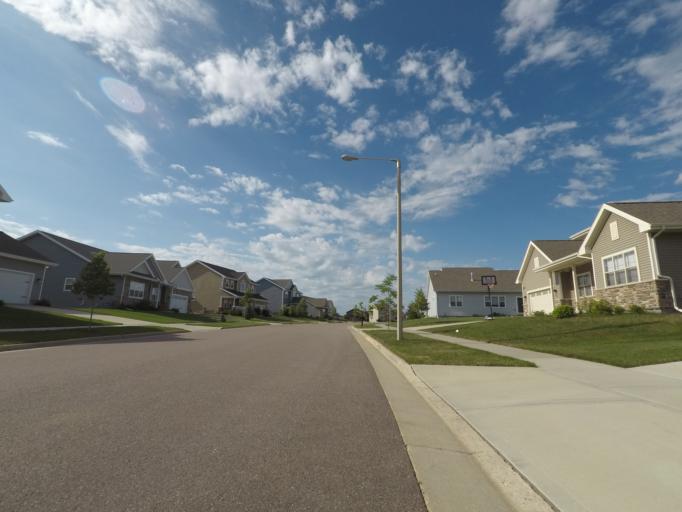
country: US
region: Wisconsin
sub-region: Dane County
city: Middleton
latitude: 43.0682
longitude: -89.5598
